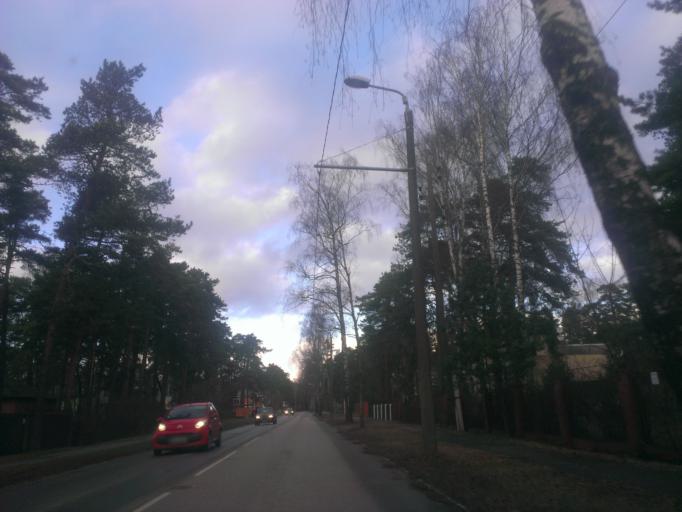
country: LV
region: Riga
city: Bolderaja
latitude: 57.0693
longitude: 24.1052
